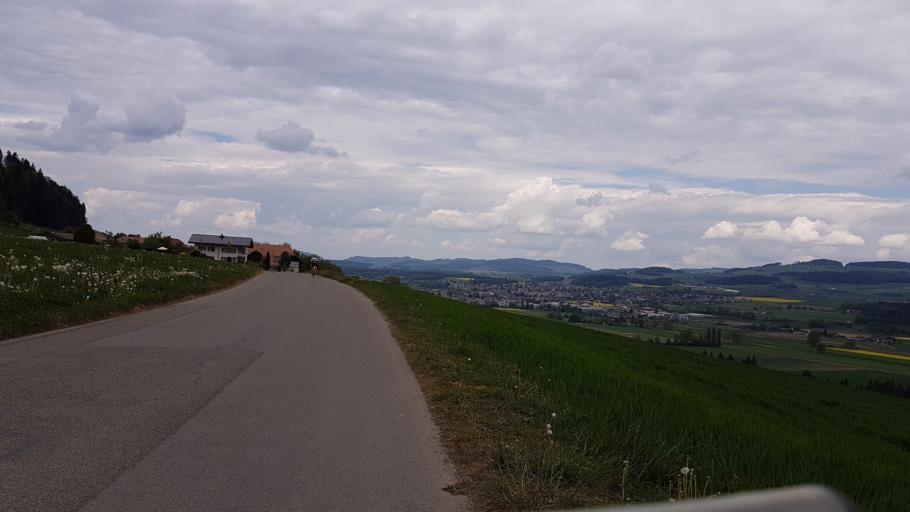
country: CH
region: Bern
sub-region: Bern-Mittelland District
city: Niederwichtrach
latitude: 46.8471
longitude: 7.5511
